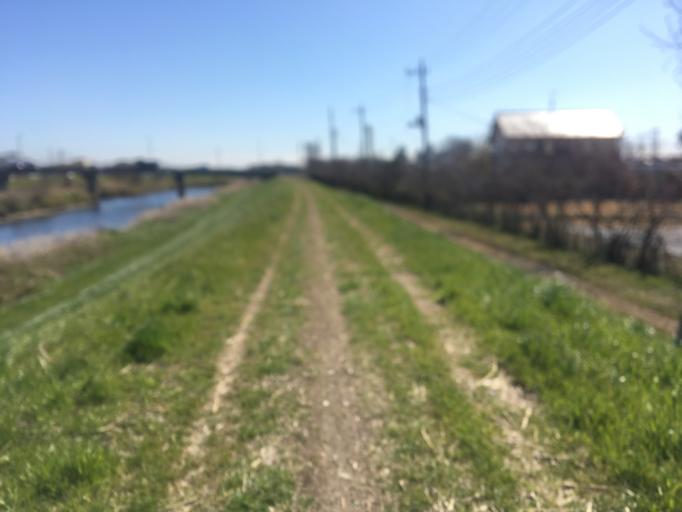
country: JP
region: Saitama
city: Asaka
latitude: 35.8209
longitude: 139.6053
